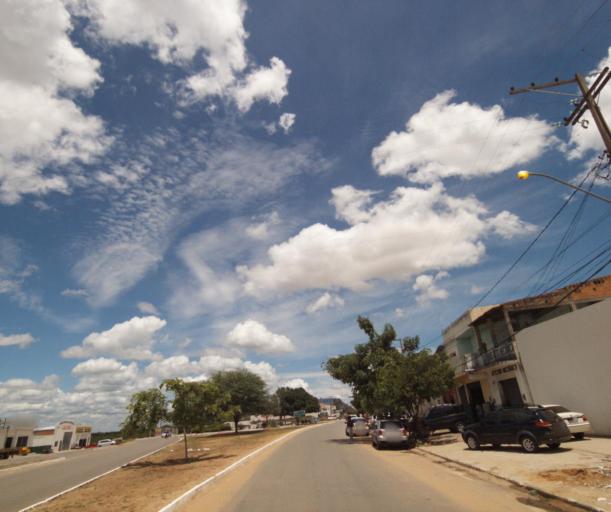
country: BR
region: Bahia
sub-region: Bom Jesus Da Lapa
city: Bom Jesus da Lapa
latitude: -13.2678
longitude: -43.4088
